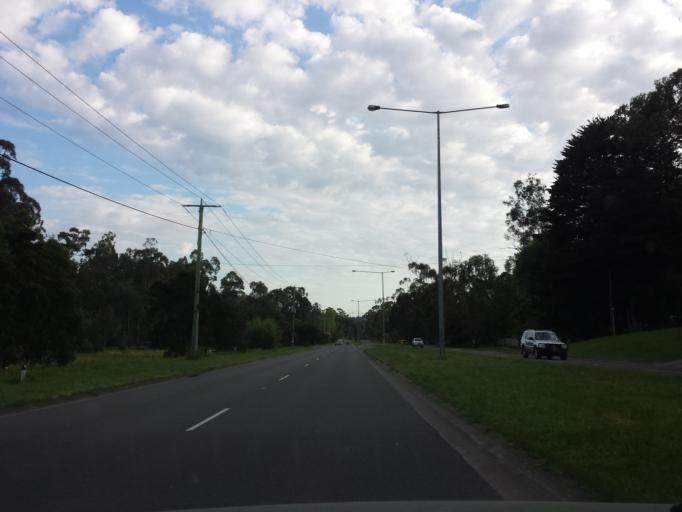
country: AU
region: Victoria
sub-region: Yarra Ranges
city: Mount Evelyn
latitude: -37.7900
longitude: 145.3611
